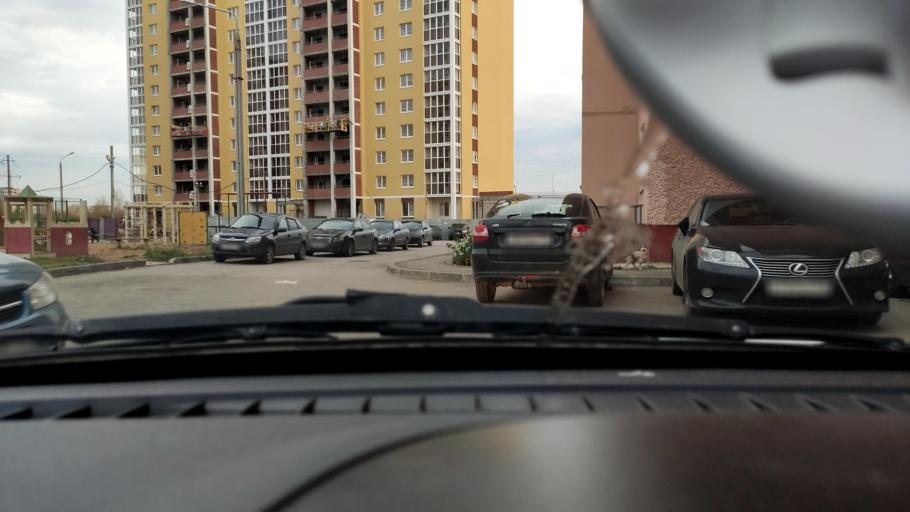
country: RU
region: Perm
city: Kondratovo
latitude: 58.0013
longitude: 56.1077
